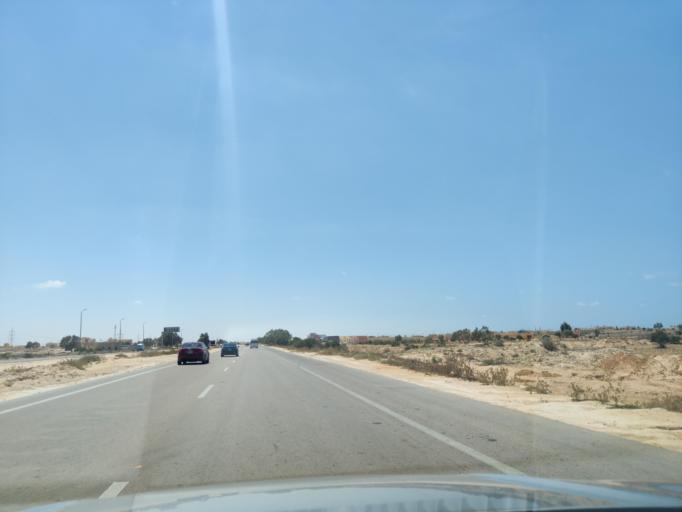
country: EG
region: Muhafazat Matruh
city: Al `Alamayn
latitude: 31.0697
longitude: 28.1333
